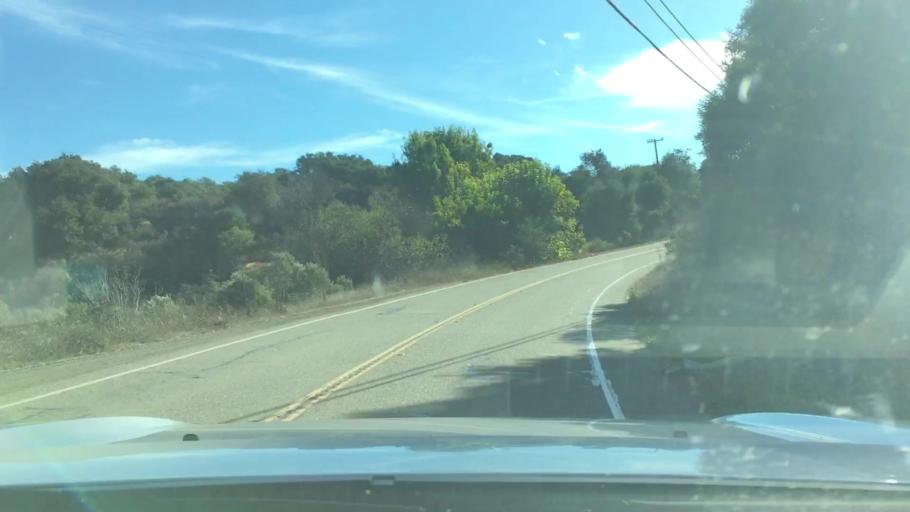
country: US
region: California
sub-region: San Luis Obispo County
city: Nipomo
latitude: 35.0766
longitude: -120.5246
